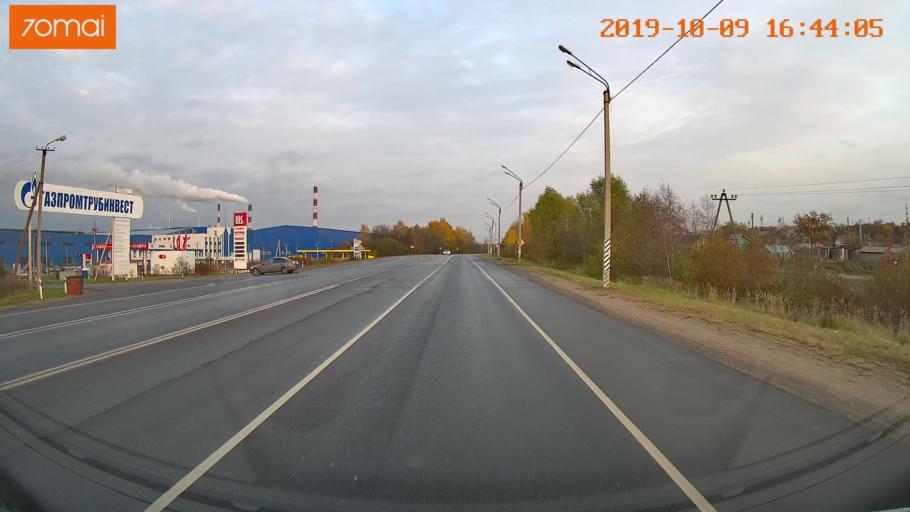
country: RU
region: Kostroma
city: Volgorechensk
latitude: 57.4522
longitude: 41.1355
